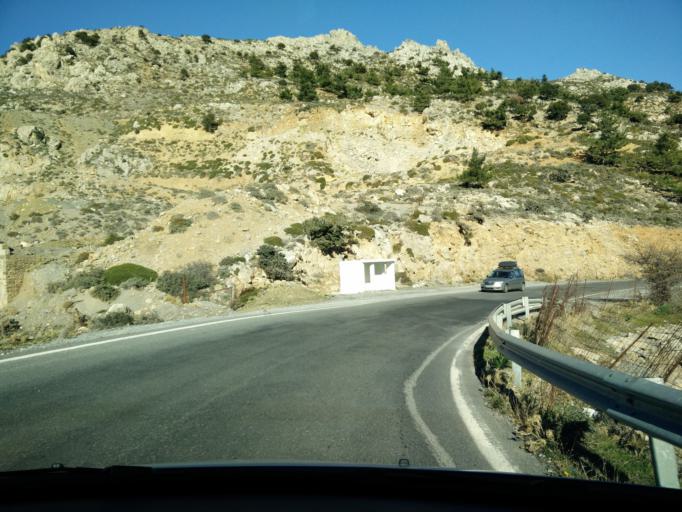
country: GR
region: Crete
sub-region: Nomos Irakleiou
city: Kastelli
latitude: 35.0448
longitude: 25.4292
